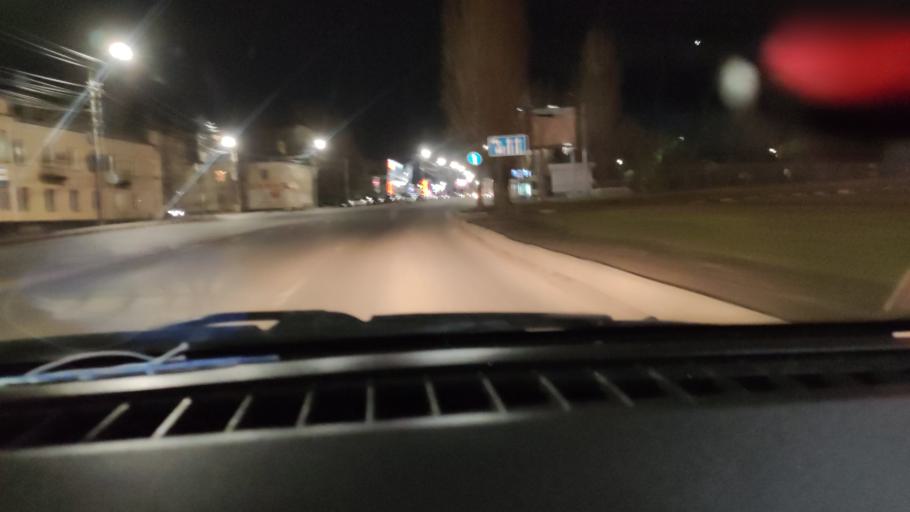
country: RU
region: Saratov
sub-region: Saratovskiy Rayon
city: Saratov
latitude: 51.5578
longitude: 46.0536
